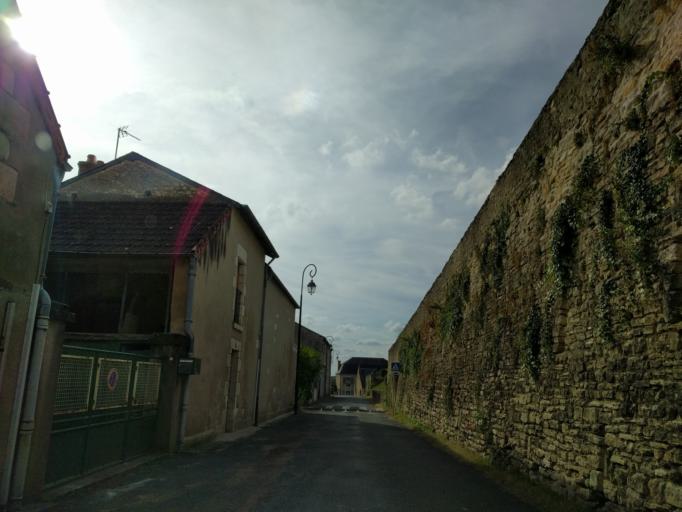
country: FR
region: Bourgogne
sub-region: Departement de la Nievre
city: La Charite-sur-Loire
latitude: 47.1788
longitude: 3.0178
